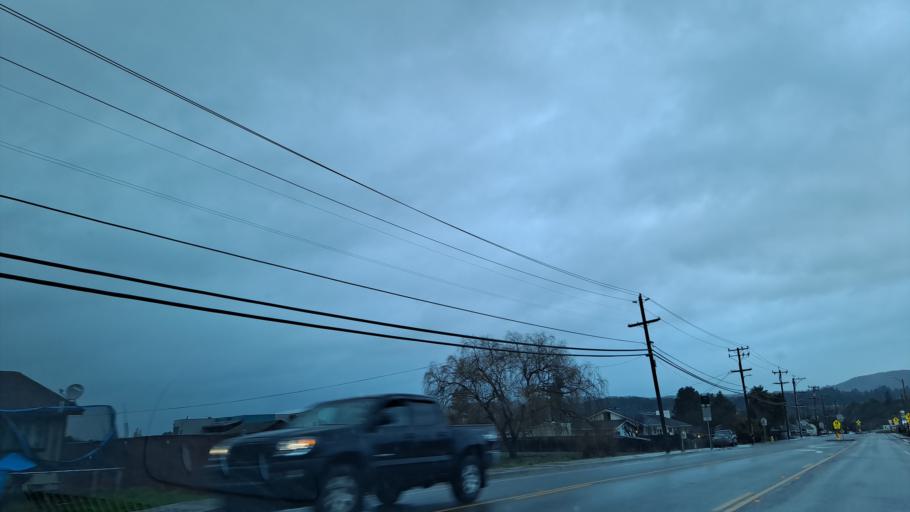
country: US
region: California
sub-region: Humboldt County
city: Fortuna
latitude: 40.5806
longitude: -124.1303
